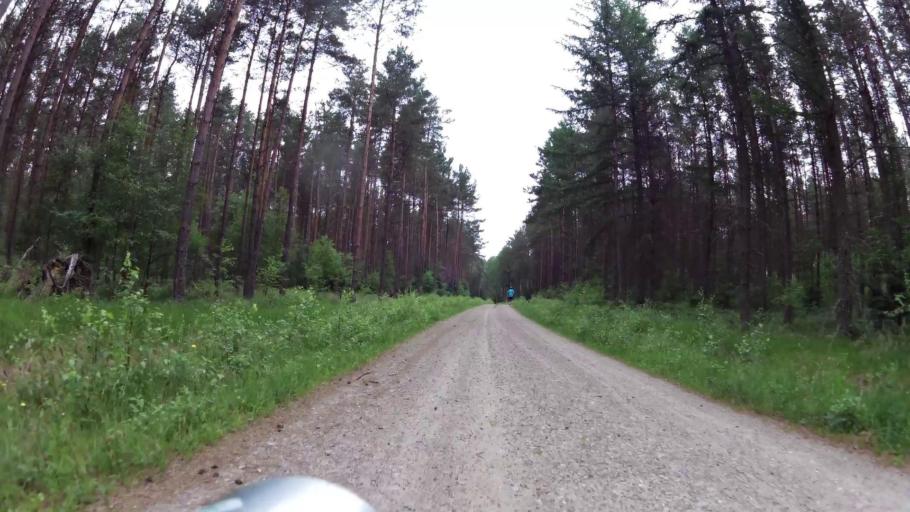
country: PL
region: West Pomeranian Voivodeship
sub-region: Powiat szczecinecki
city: Bialy Bor
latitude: 53.9279
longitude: 16.8356
